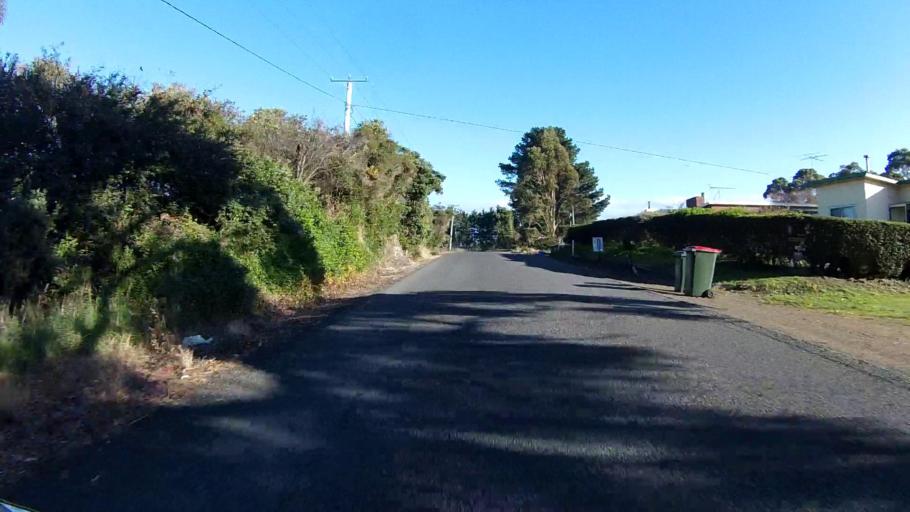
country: AU
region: Tasmania
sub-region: Clarence
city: Sandford
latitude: -43.1679
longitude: 147.8594
